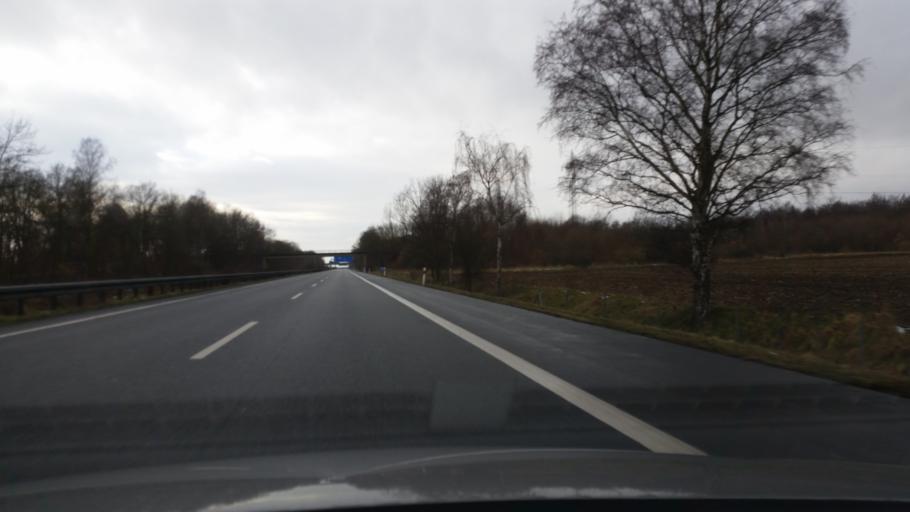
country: DE
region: Lower Saxony
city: Laatzen
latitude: 52.3048
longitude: 9.8623
